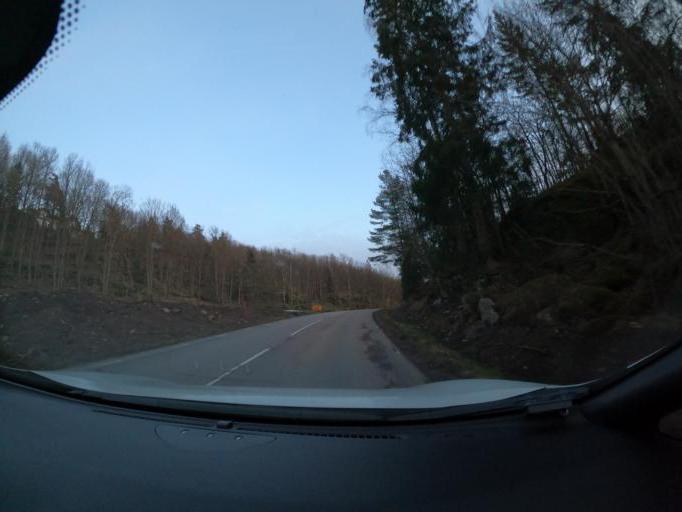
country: SE
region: Vaestra Goetaland
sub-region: Harryda Kommun
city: Landvetter
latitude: 57.6390
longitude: 12.1806
